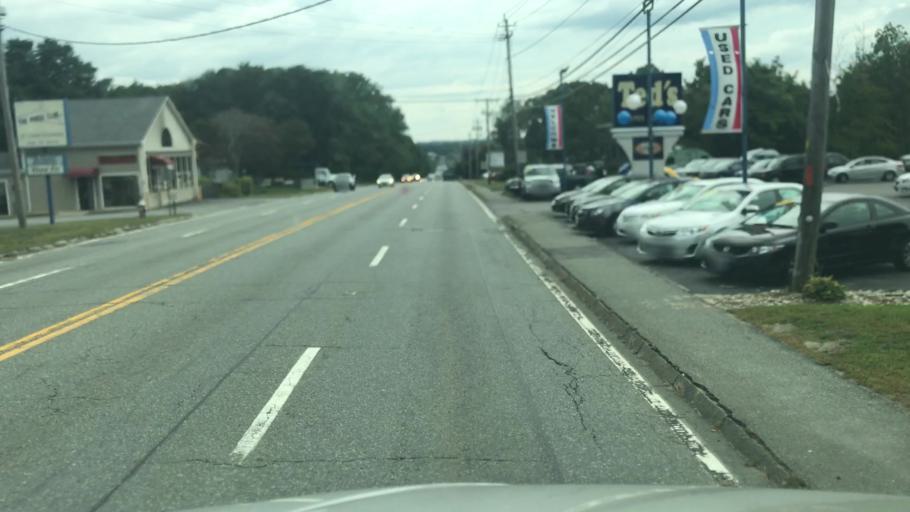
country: US
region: Massachusetts
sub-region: Bristol County
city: Swansea
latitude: 41.7345
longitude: -71.1763
